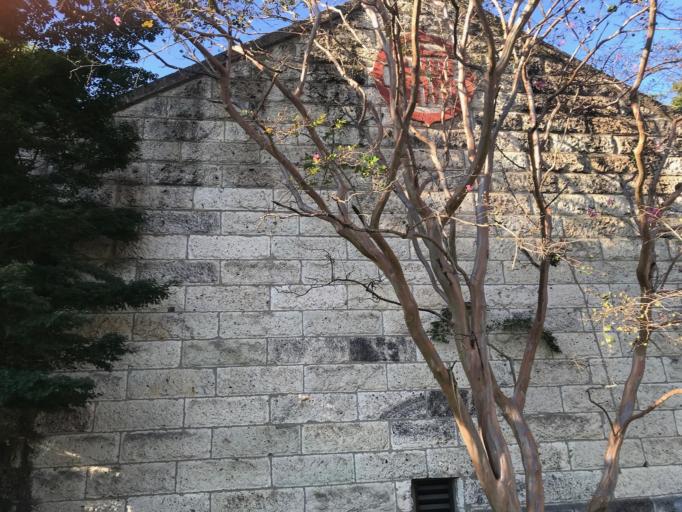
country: JP
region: Tochigi
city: Kanuma
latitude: 36.5688
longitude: 139.7525
